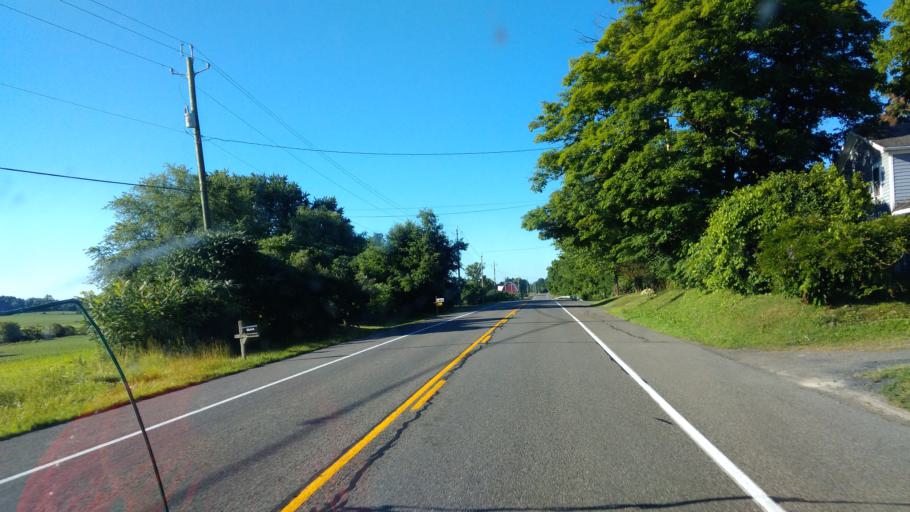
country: US
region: New York
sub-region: Ontario County
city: Phelps
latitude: 42.9709
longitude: -76.9776
